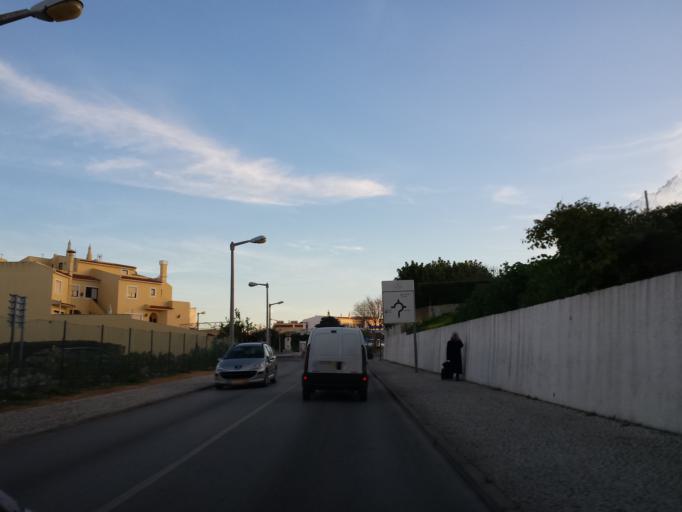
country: PT
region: Faro
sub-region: Lagos
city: Lagos
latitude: 37.0945
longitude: -8.6748
